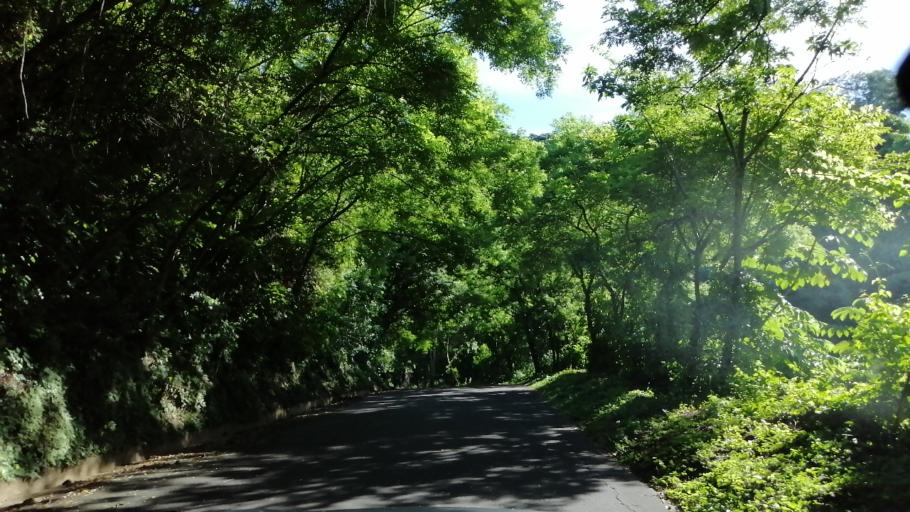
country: SV
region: Morazan
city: Cacaopera
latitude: 13.7820
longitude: -88.0354
